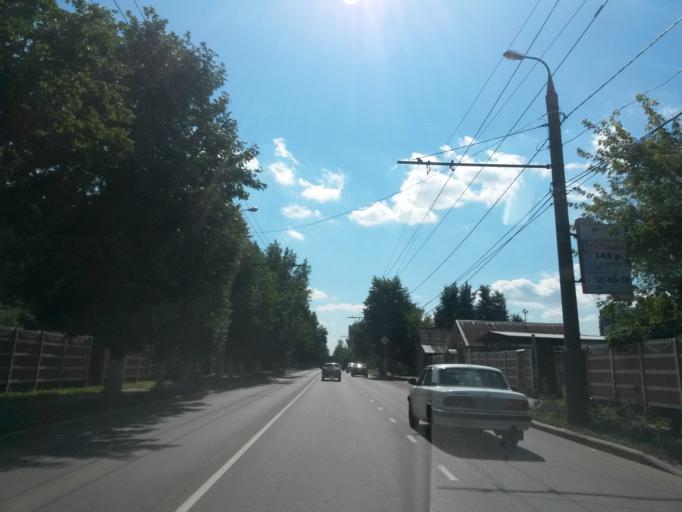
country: RU
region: Ivanovo
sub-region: Gorod Ivanovo
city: Ivanovo
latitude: 56.9899
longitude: 40.9846
